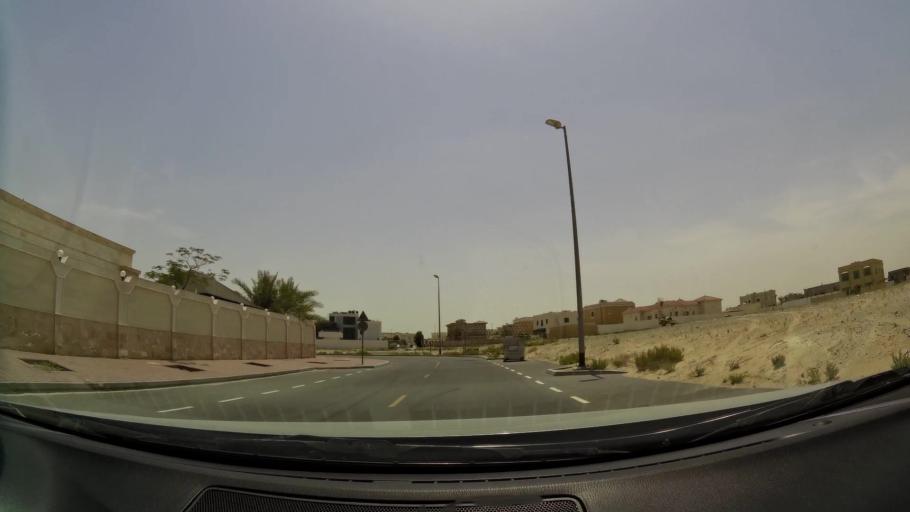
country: AE
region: Ash Shariqah
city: Sharjah
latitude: 25.1923
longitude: 55.4191
